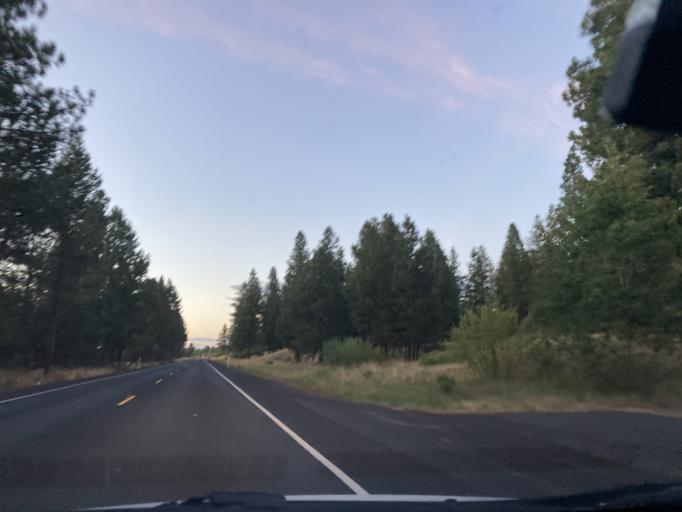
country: US
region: Oregon
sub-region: Deschutes County
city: Three Rivers
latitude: 43.8448
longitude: -121.4413
